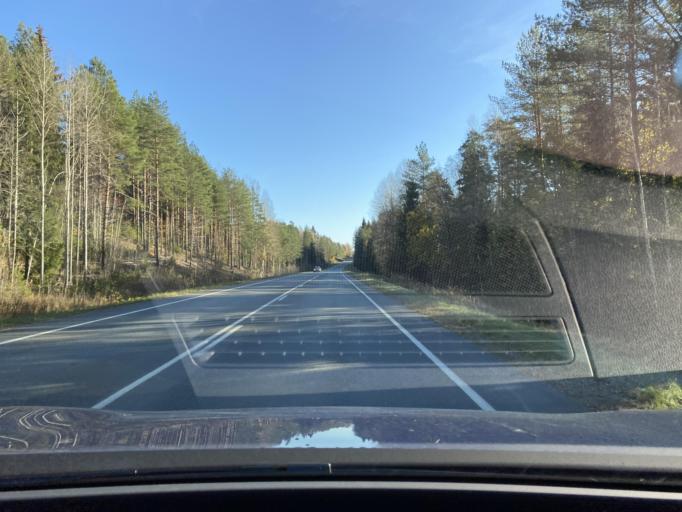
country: FI
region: Haeme
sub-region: Haemeenlinna
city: Parola
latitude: 61.0154
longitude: 24.3689
